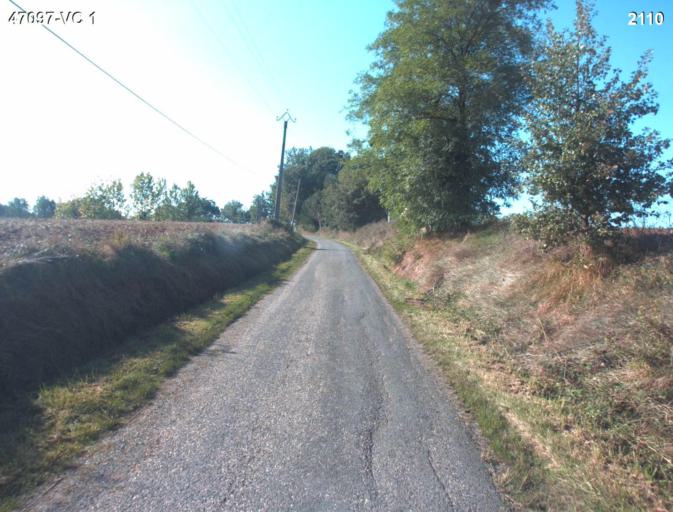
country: FR
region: Aquitaine
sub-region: Departement du Lot-et-Garonne
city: Vianne
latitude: 44.2071
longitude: 0.3584
